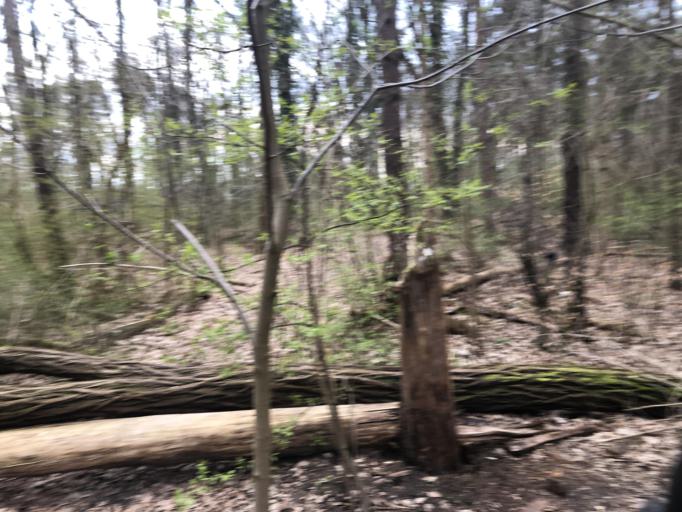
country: DE
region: Berlin
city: Frohnau
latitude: 52.6475
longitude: 13.2907
